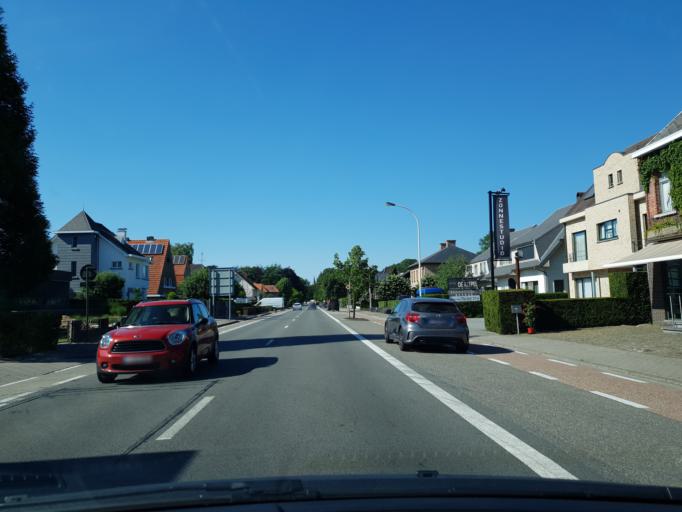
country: BE
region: Flanders
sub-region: Provincie Antwerpen
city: Beerse
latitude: 51.3117
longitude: 4.8561
